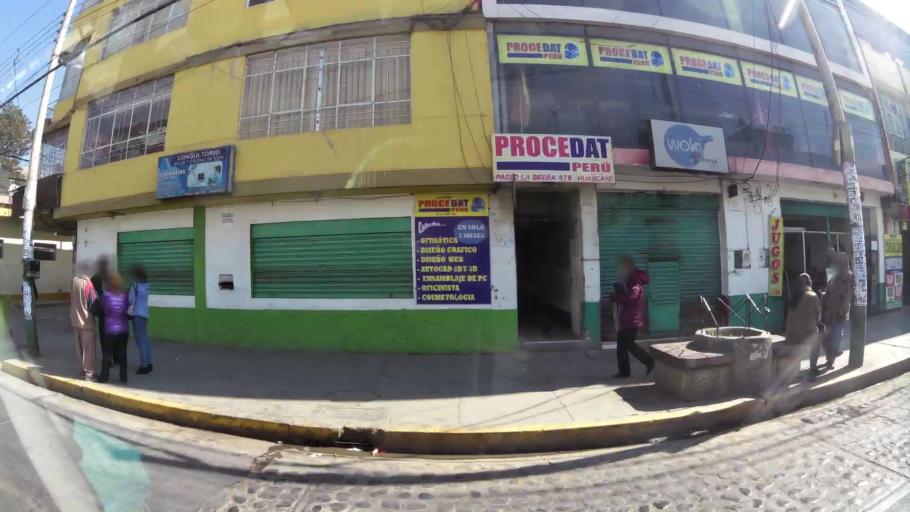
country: PE
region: Junin
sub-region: Provincia de Huancayo
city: El Tambo
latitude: -12.0704
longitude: -75.2135
